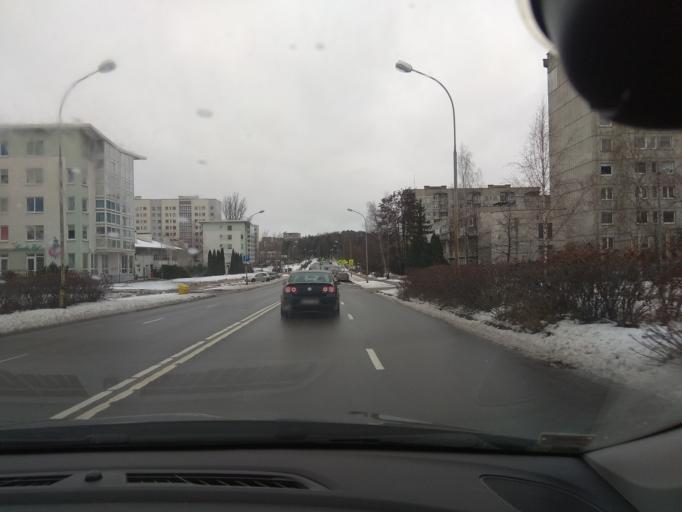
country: LT
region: Vilnius County
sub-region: Vilnius
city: Fabijoniskes
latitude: 54.7308
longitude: 25.2341
